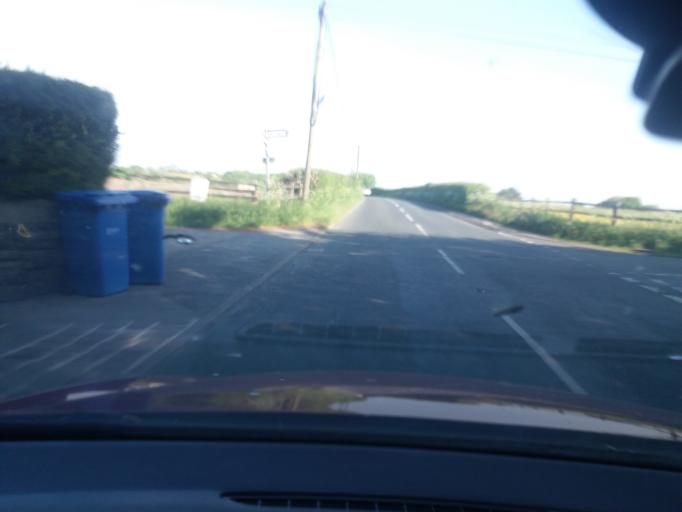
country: GB
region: England
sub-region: Borough of Wigan
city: Haigh
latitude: 53.6212
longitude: -2.5826
